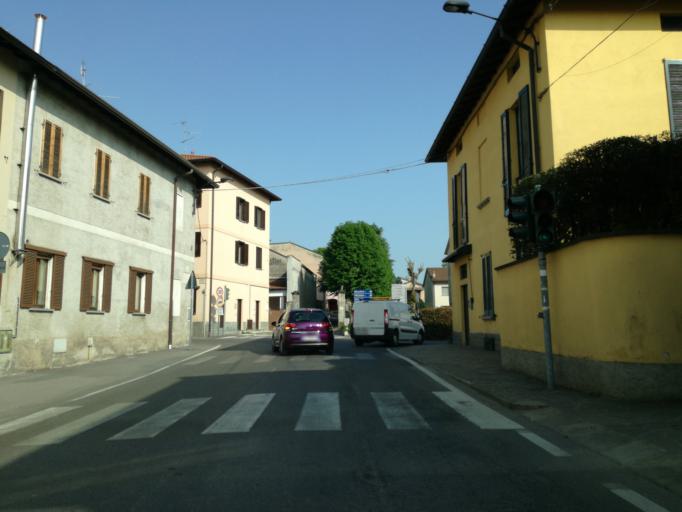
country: IT
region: Lombardy
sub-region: Provincia di Lecco
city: Verderio Inferiore
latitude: 45.6618
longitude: 9.4338
